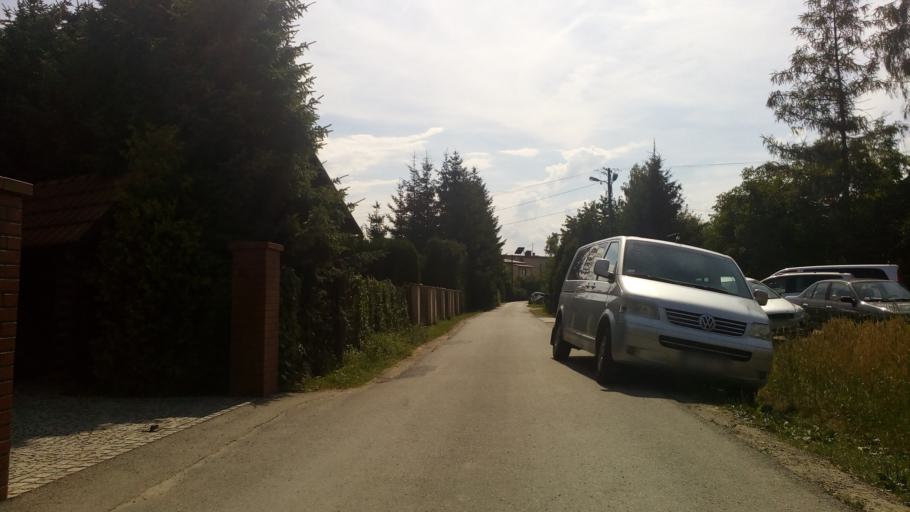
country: PL
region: Lesser Poland Voivodeship
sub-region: Powiat nowosadecki
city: Stary Sacz
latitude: 49.5701
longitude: 20.6334
